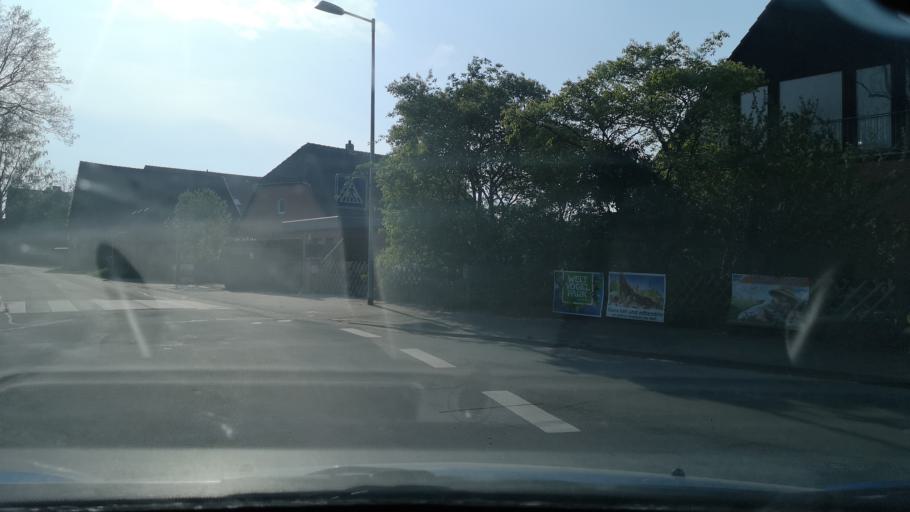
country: DE
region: Lower Saxony
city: Garbsen-Mitte
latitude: 52.4496
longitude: 9.6592
